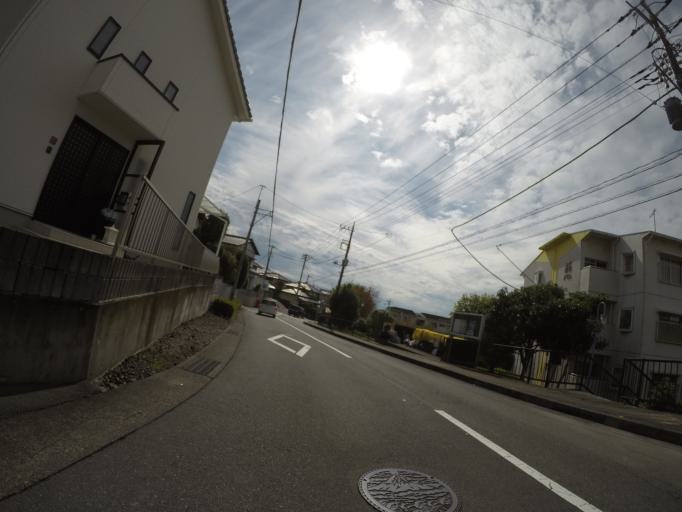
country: JP
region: Shizuoka
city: Fuji
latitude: 35.1854
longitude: 138.6915
